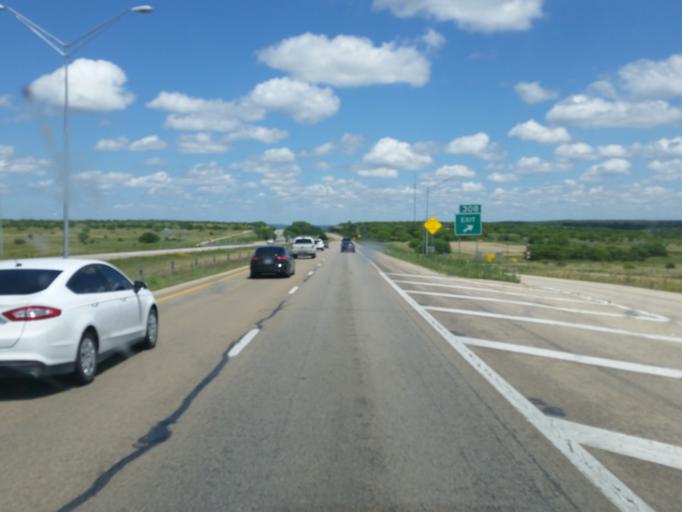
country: US
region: Texas
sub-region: Callahan County
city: Baird
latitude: 32.3989
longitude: -99.3761
